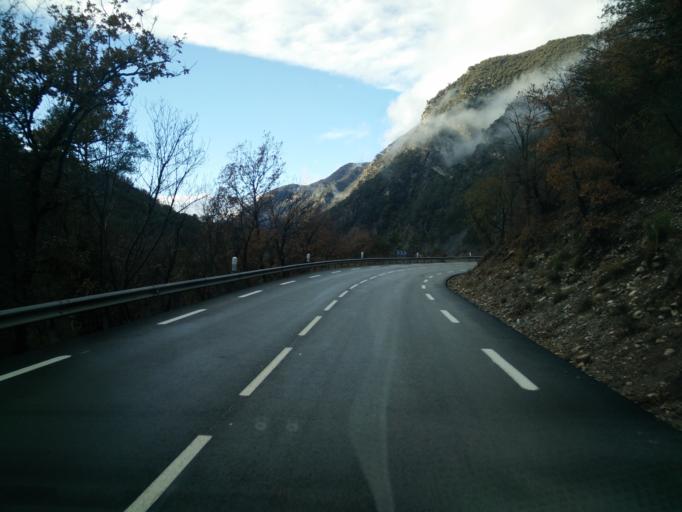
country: FR
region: Provence-Alpes-Cote d'Azur
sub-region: Departement des Alpes-Maritimes
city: Gilette
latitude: 43.9397
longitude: 7.0599
